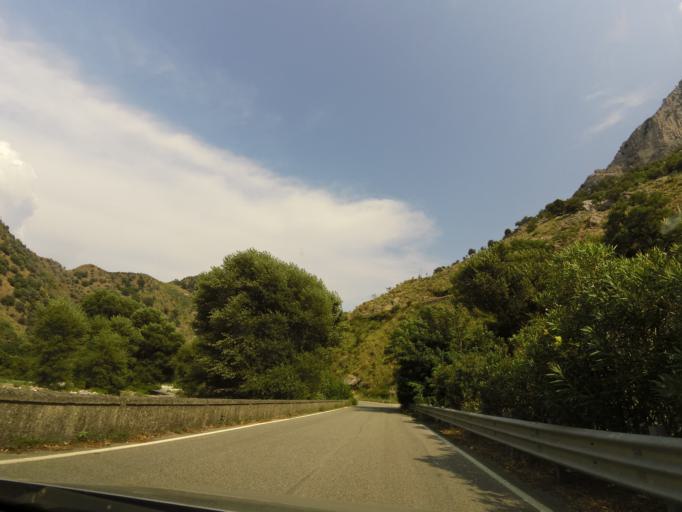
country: IT
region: Calabria
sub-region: Provincia di Reggio Calabria
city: Stilo
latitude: 38.4872
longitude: 16.4640
